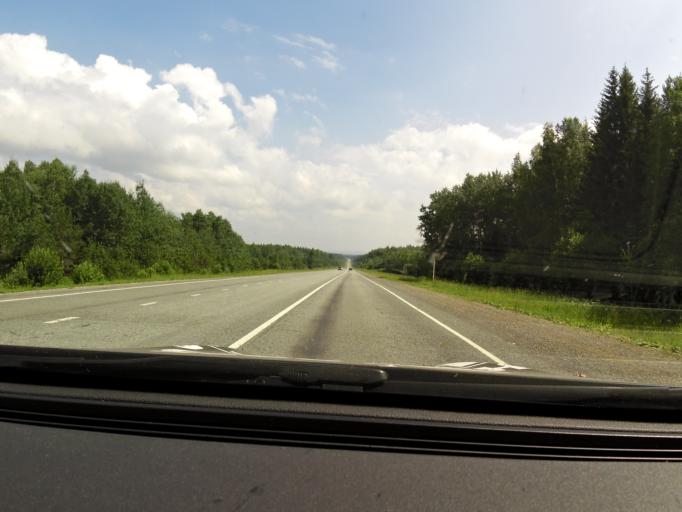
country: RU
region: Sverdlovsk
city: Achit
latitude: 56.8238
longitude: 57.8017
